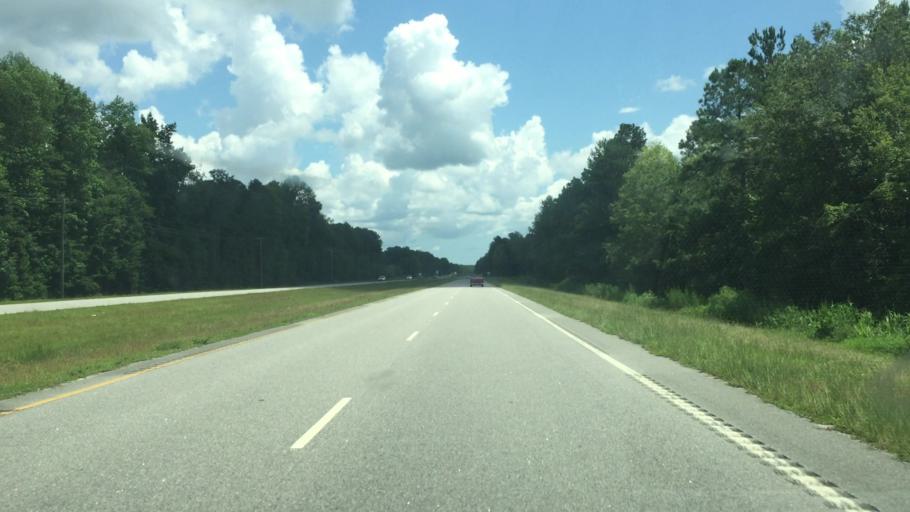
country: US
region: South Carolina
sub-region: Horry County
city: Loris
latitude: 34.0428
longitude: -78.8253
